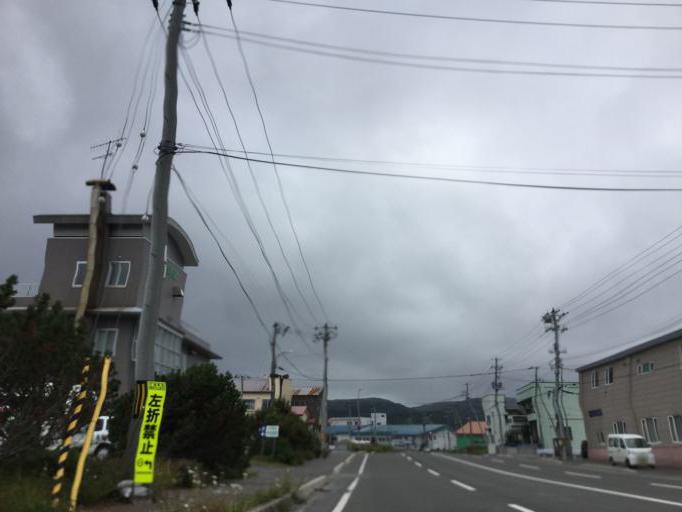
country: JP
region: Hokkaido
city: Wakkanai
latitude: 45.4003
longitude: 141.6929
